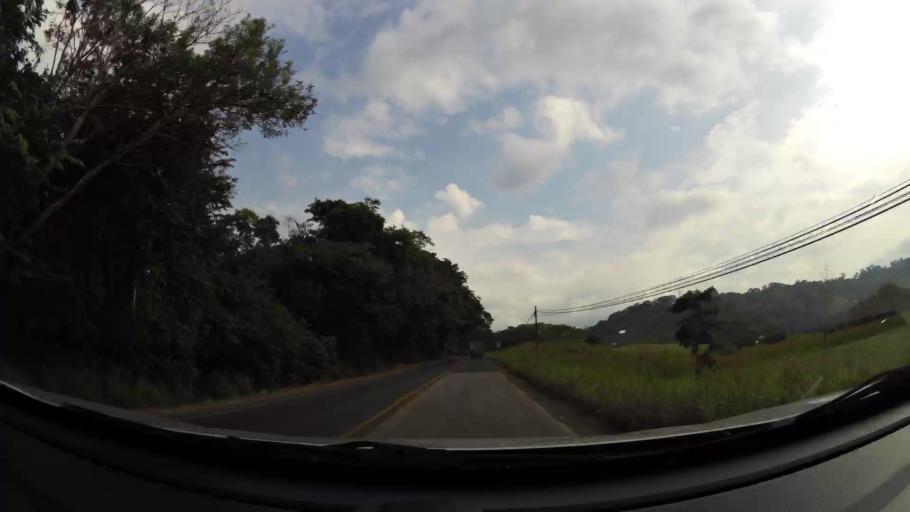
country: CR
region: Guanacaste
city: Juntas
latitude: 10.1951
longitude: -84.9525
